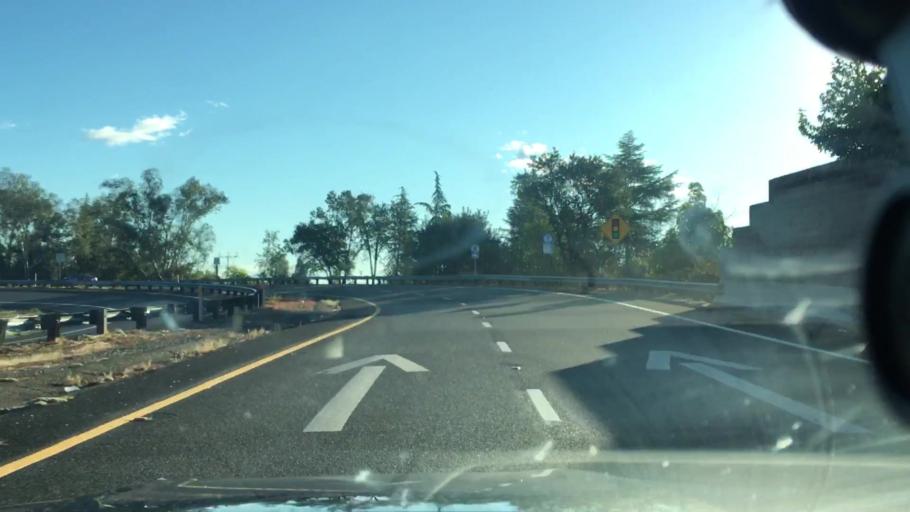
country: US
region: California
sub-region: Sacramento County
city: Antelope
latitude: 38.7064
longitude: -121.3092
